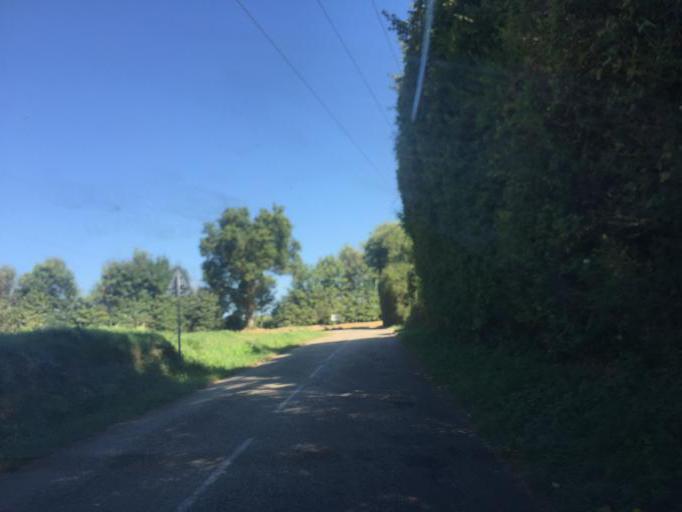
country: FR
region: Rhone-Alpes
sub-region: Departement de l'Ain
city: Saint-Maurice-de-Beynost
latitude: 45.8444
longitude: 4.9750
